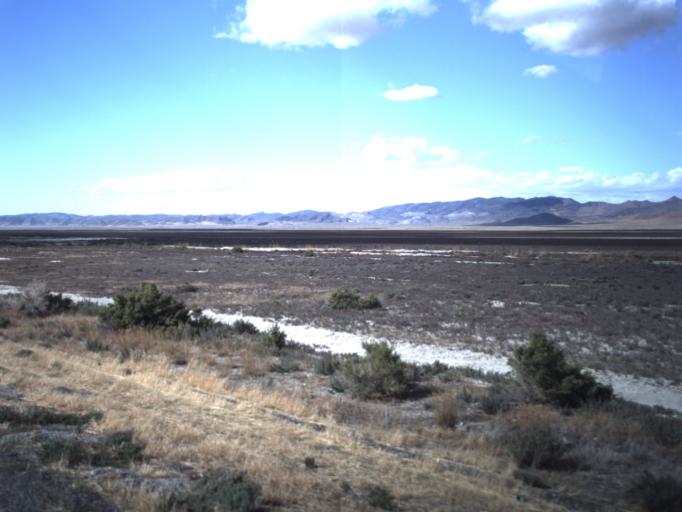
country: US
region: Utah
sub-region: Millard County
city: Delta
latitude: 39.0339
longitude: -112.7741
